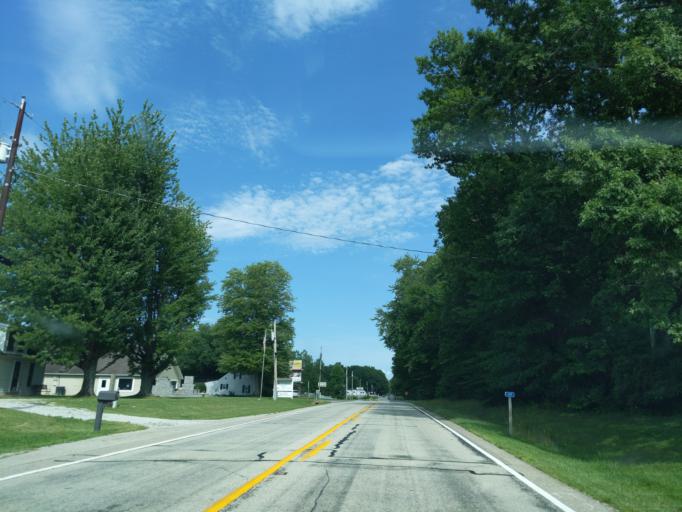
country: US
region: Indiana
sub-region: Ripley County
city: Sunman
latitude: 39.2783
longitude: -85.1327
